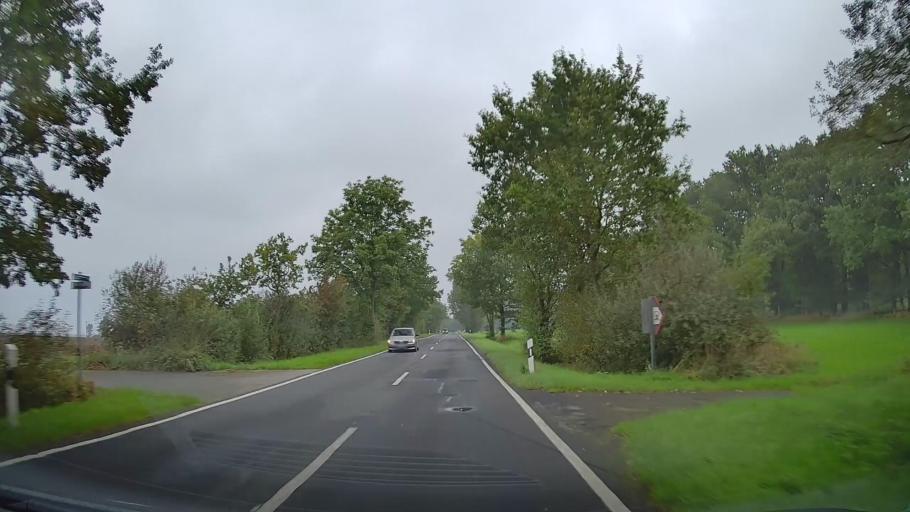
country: DE
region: Mecklenburg-Vorpommern
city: Neubukow
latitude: 54.0820
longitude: 11.6315
